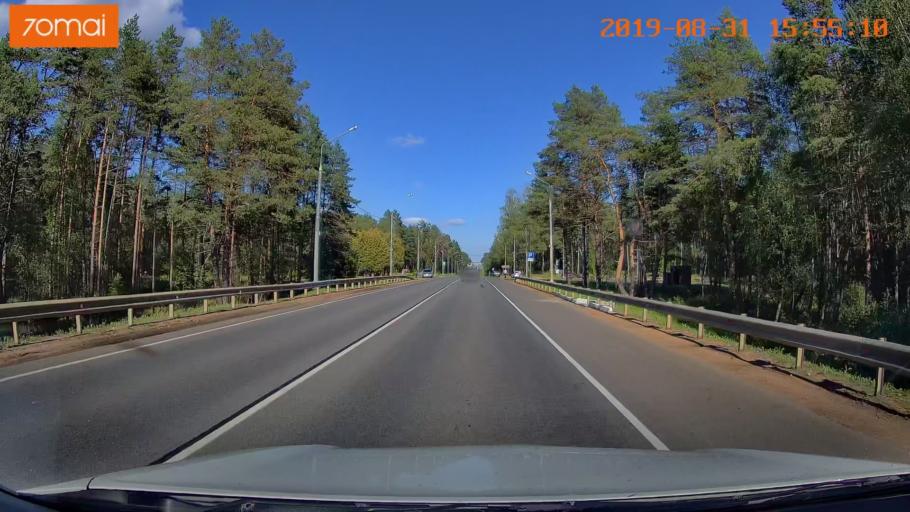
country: RU
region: Kaluga
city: Yukhnov
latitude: 54.7235
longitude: 35.1648
